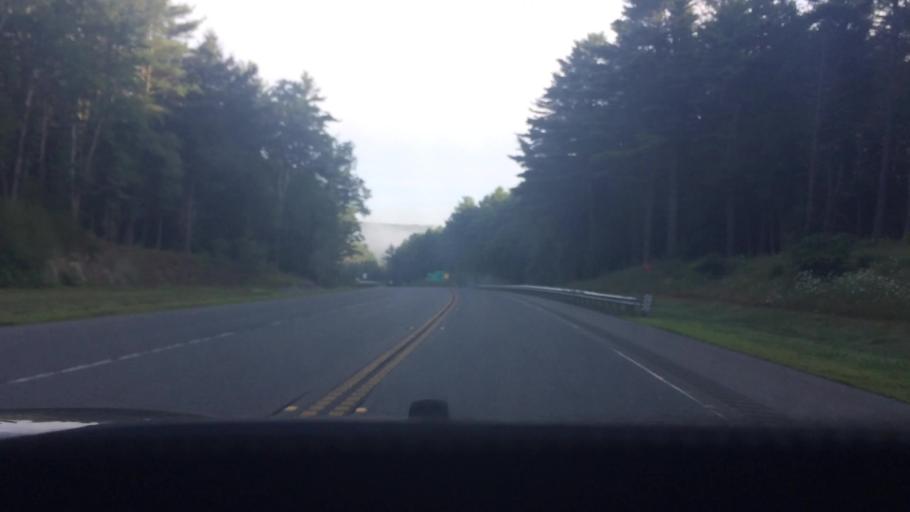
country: US
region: Massachusetts
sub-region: Franklin County
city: Orange
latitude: 42.5853
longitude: -72.3265
